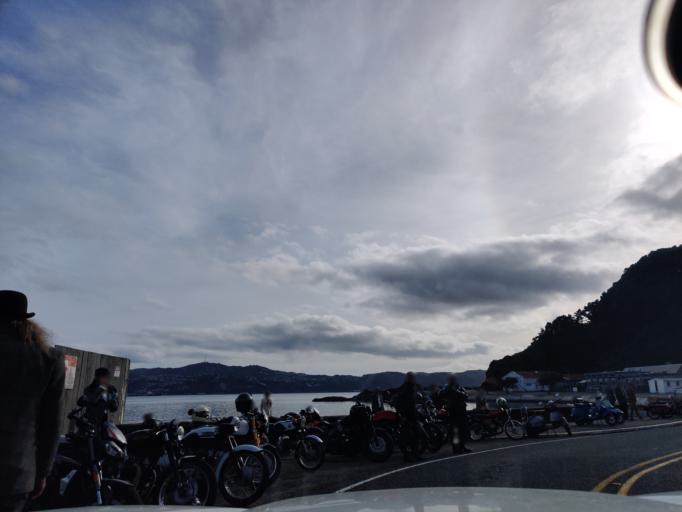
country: NZ
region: Wellington
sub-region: Wellington City
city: Wellington
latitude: -41.2939
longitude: 174.8217
